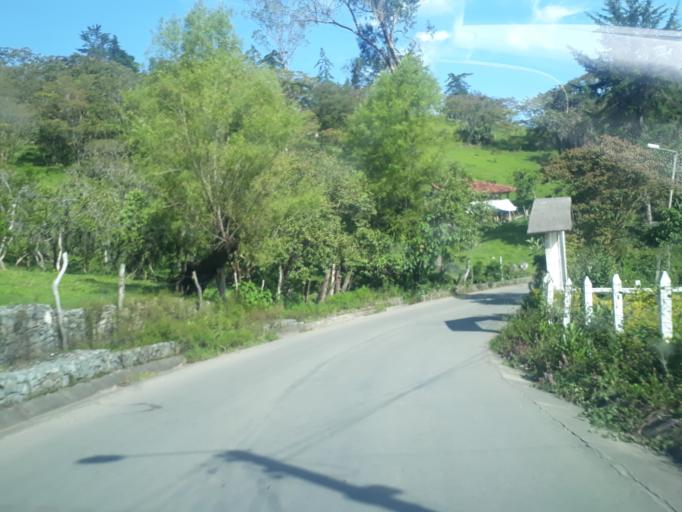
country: CO
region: Santander
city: Velez
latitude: 6.0229
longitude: -73.6648
